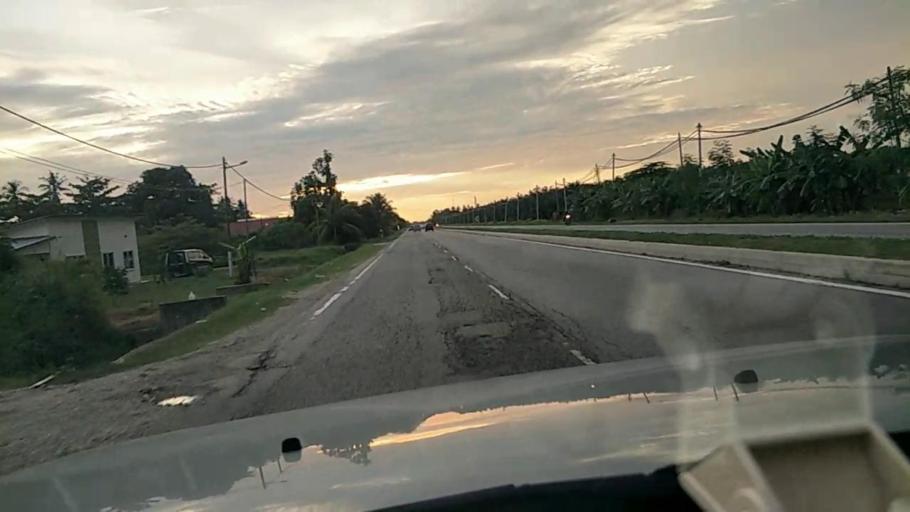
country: MY
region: Perak
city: Kampong Dungun
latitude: 3.1418
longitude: 101.3618
